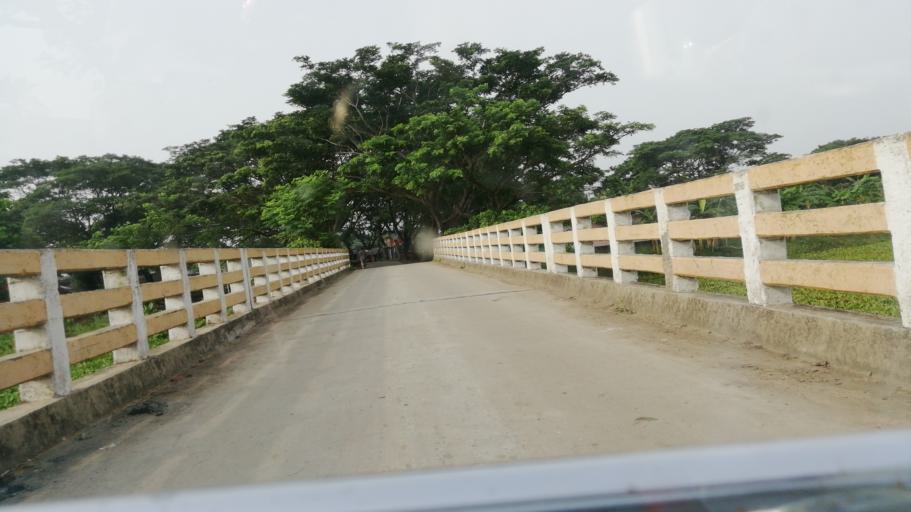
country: BD
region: Khulna
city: Bhatpara Abhaynagar
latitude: 23.0381
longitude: 89.3053
